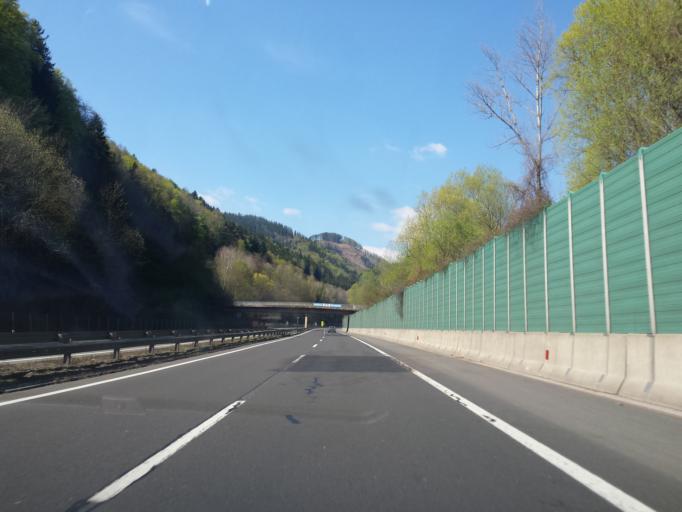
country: AT
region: Styria
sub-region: Politischer Bezirk Graz-Umgebung
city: Ubelbach
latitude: 47.2182
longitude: 15.2836
